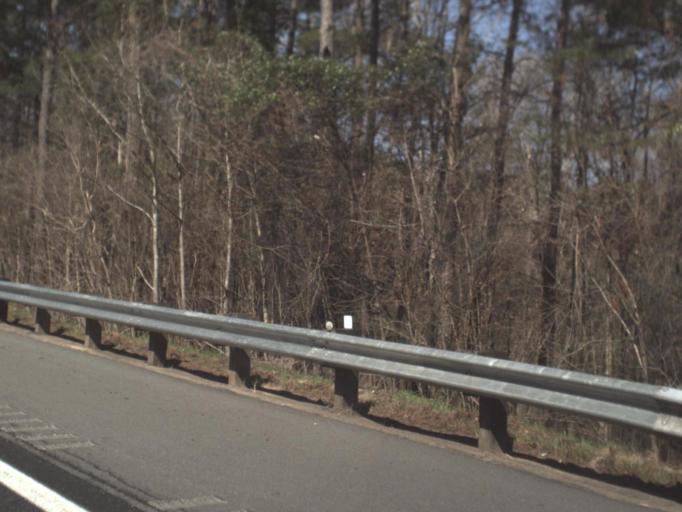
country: US
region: Florida
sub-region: Gadsden County
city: Chattahoochee
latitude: 30.6334
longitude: -84.8844
